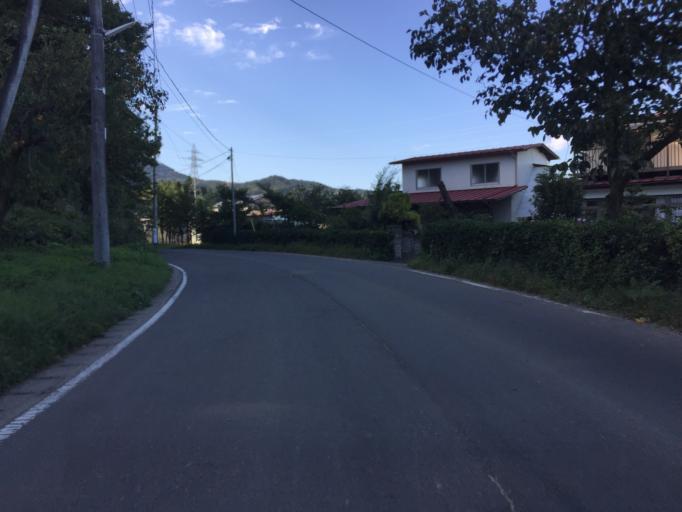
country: JP
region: Miyagi
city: Marumori
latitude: 37.9001
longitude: 140.7690
